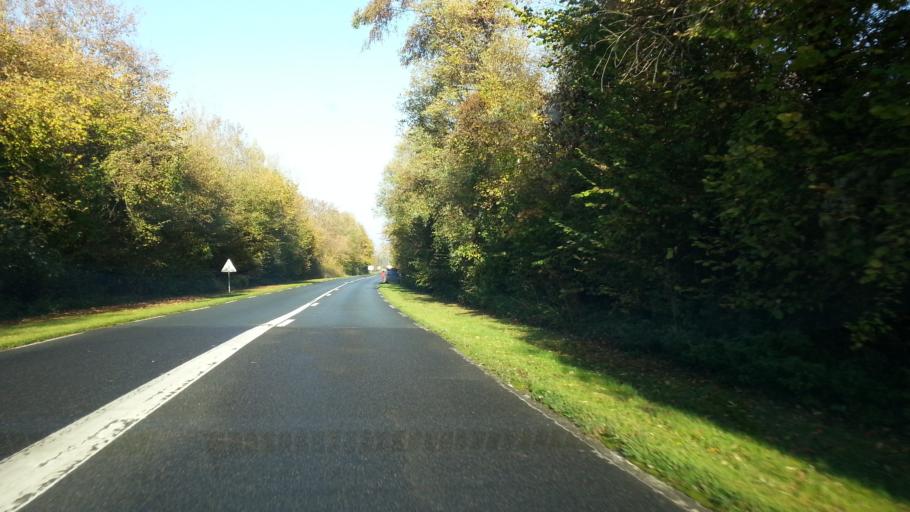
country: FR
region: Picardie
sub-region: Departement de l'Oise
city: Balagny-sur-Therain
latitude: 49.3053
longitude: 2.3295
